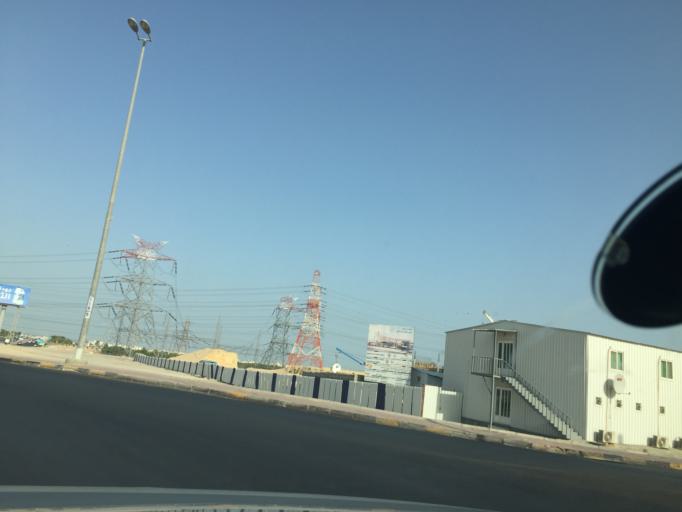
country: KW
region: Mubarak al Kabir
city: Mubarak al Kabir
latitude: 29.2041
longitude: 48.0515
